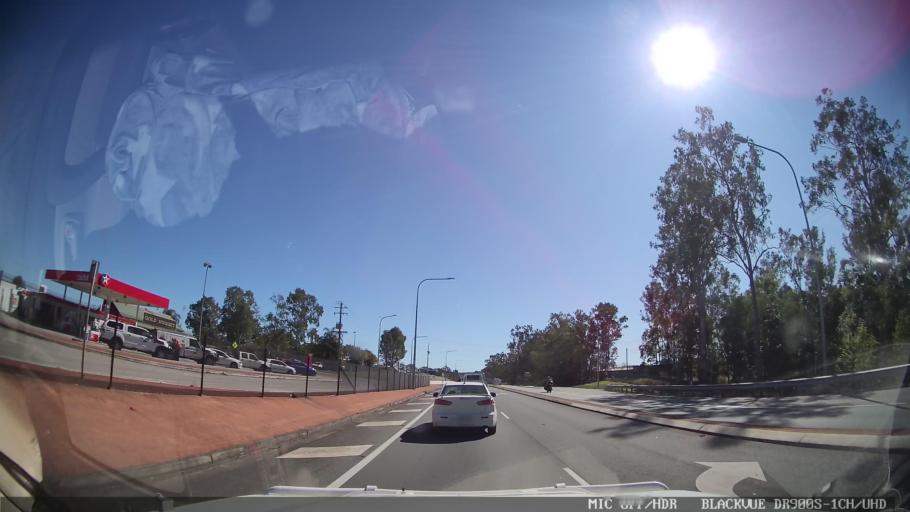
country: AU
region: Queensland
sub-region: Gympie Regional Council
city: Monkland
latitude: -26.2386
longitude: 152.6996
